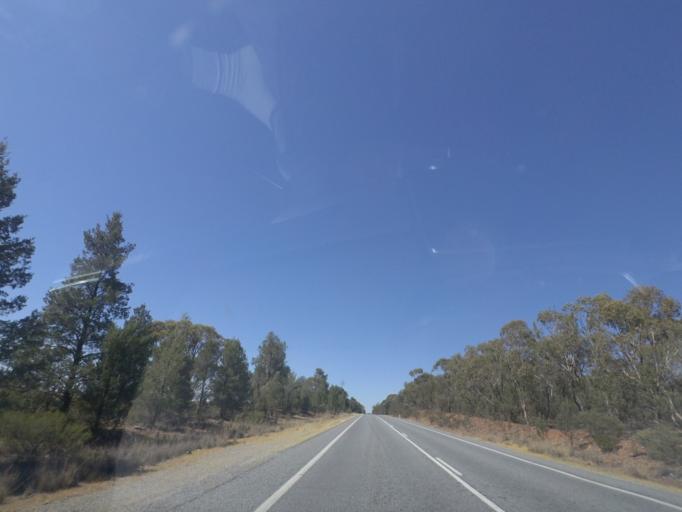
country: AU
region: New South Wales
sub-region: Narrandera
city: Narrandera
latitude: -34.4306
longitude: 146.8433
